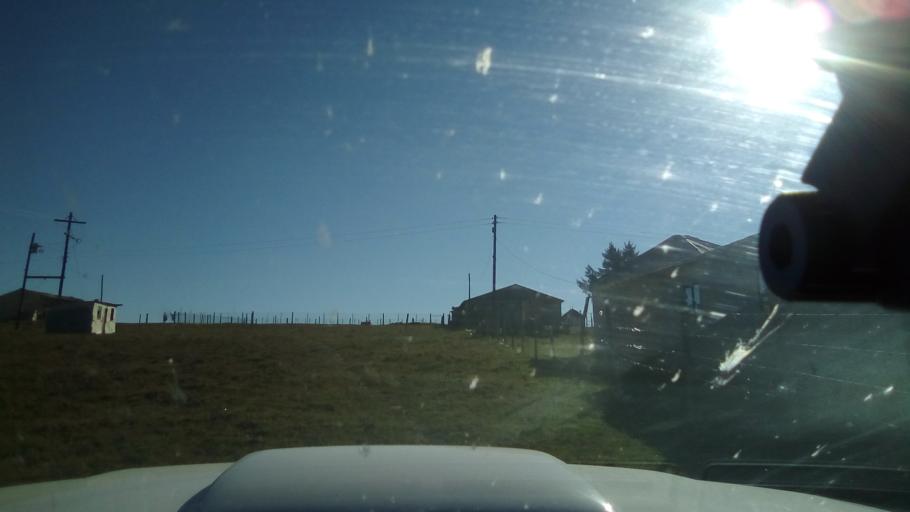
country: ZA
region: Eastern Cape
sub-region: Buffalo City Metropolitan Municipality
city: Bhisho
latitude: -32.9489
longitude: 27.2887
